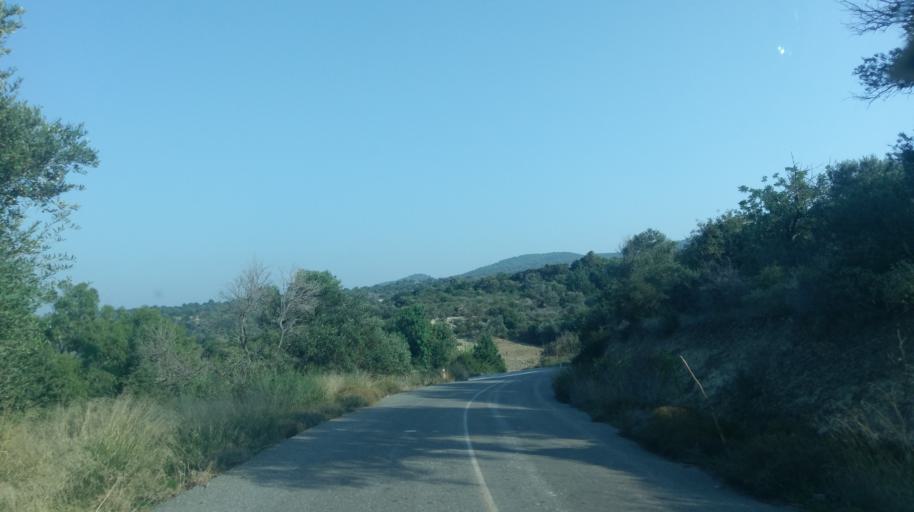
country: CY
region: Ammochostos
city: Leonarisso
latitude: 35.5501
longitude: 34.2275
